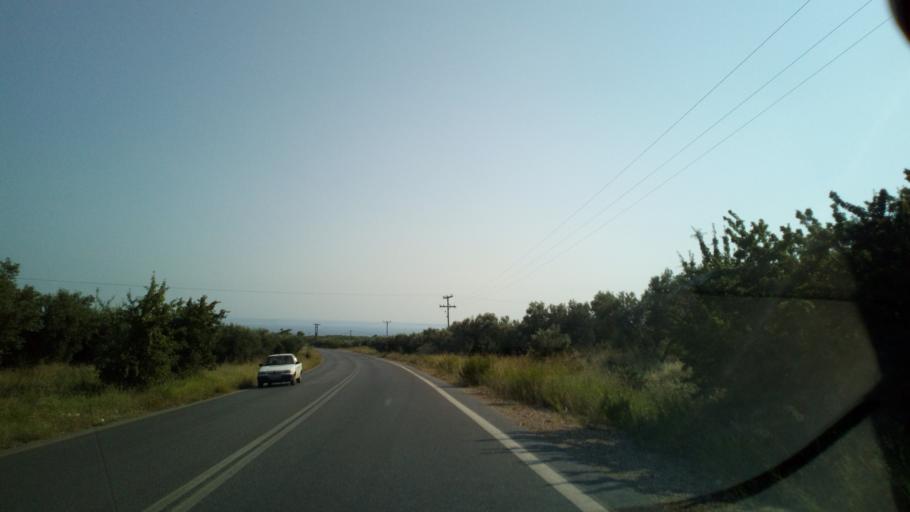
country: GR
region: Central Macedonia
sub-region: Nomos Chalkidikis
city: Kalyves Polygyrou
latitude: 40.2988
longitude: 23.4321
